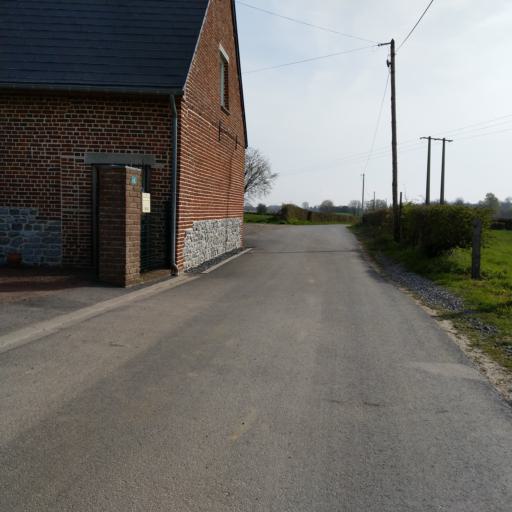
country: FR
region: Nord-Pas-de-Calais
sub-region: Departement du Nord
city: La Longueville
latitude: 50.3286
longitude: 3.8796
